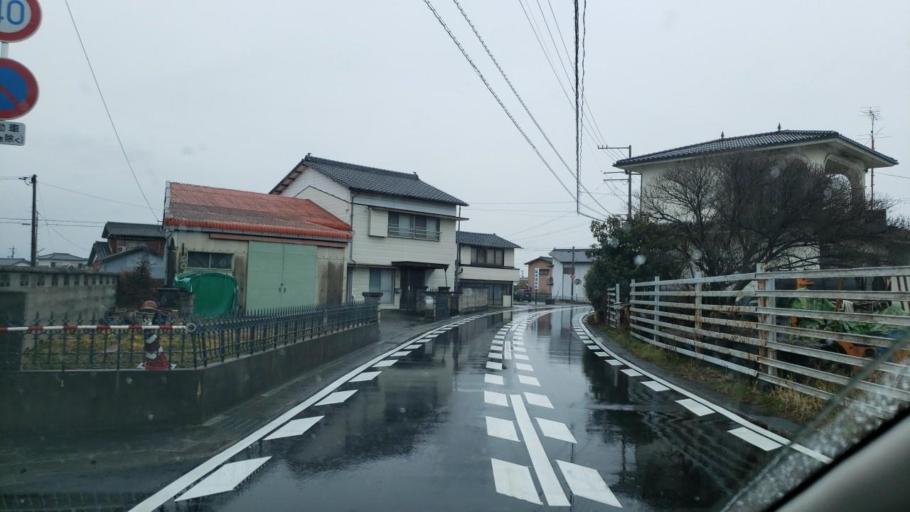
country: JP
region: Tokushima
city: Kamojimacho-jogejima
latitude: 34.0999
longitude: 134.3954
